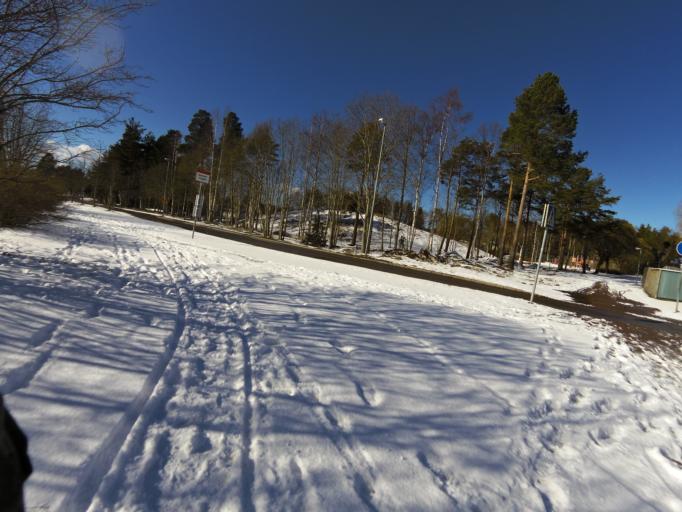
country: SE
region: Gaevleborg
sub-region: Gavle Kommun
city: Gavle
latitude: 60.6626
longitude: 17.2153
